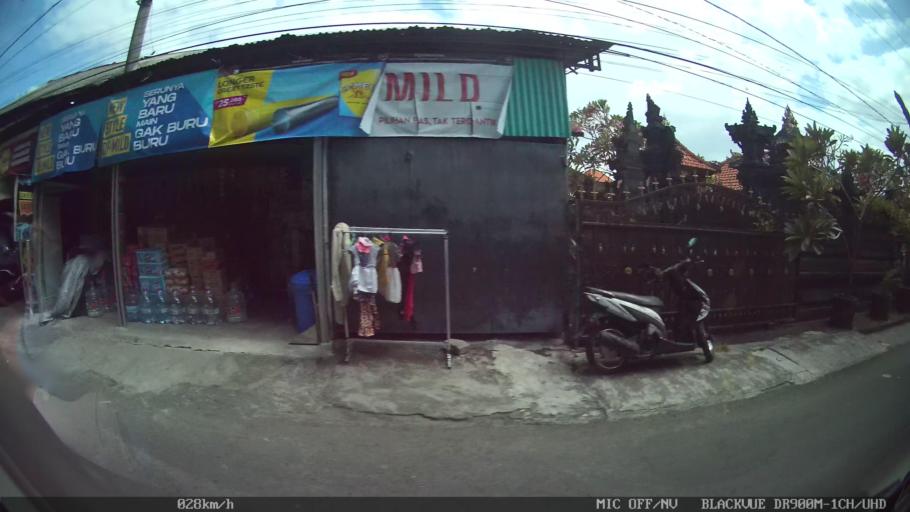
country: ID
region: Bali
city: Karyadharma
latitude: -8.6805
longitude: 115.1841
